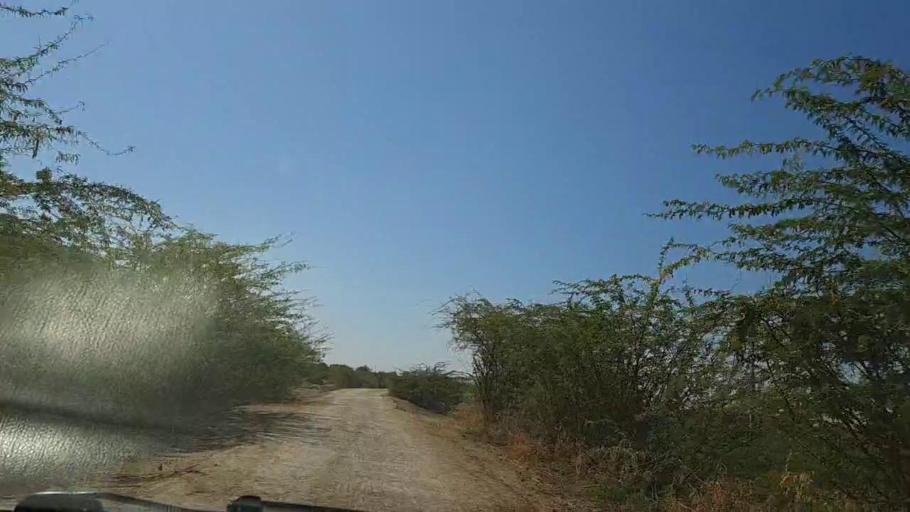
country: PK
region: Sindh
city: Dhoro Naro
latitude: 25.4773
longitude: 69.5389
